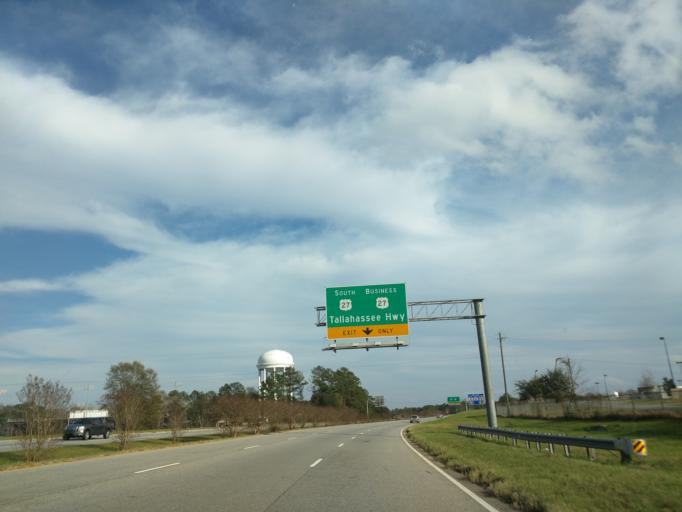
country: US
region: Georgia
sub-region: Decatur County
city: Bainbridge
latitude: 30.8920
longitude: -84.5729
